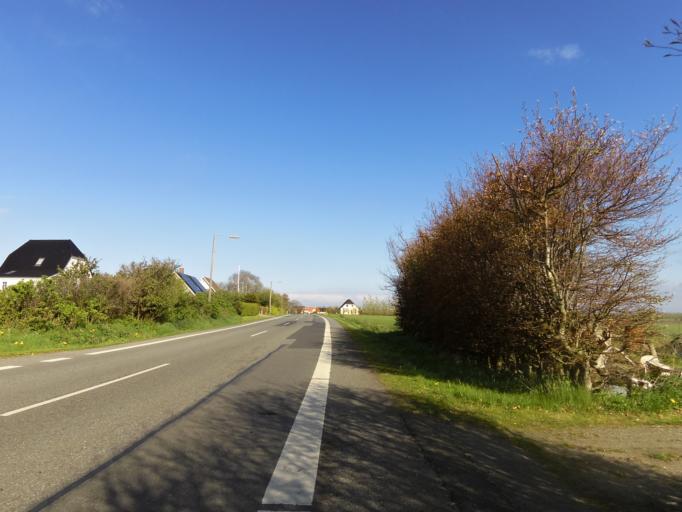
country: DK
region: South Denmark
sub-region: Tonder Kommune
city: Sherrebek
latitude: 55.1562
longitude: 8.8227
